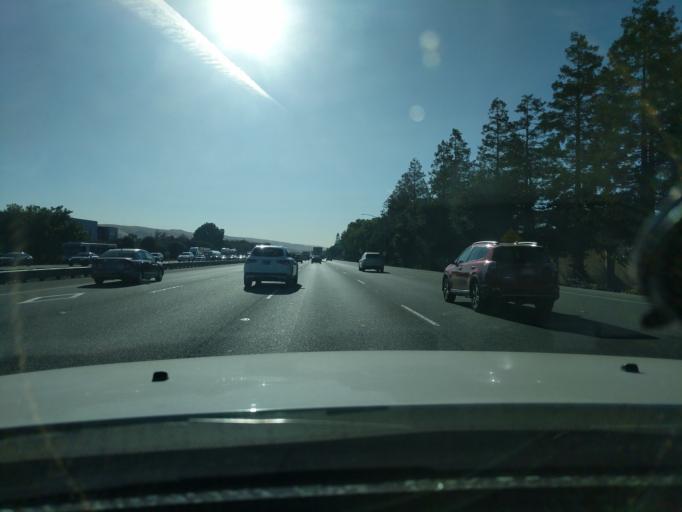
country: US
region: California
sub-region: Santa Clara County
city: Seven Trees
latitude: 37.2551
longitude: -121.7935
